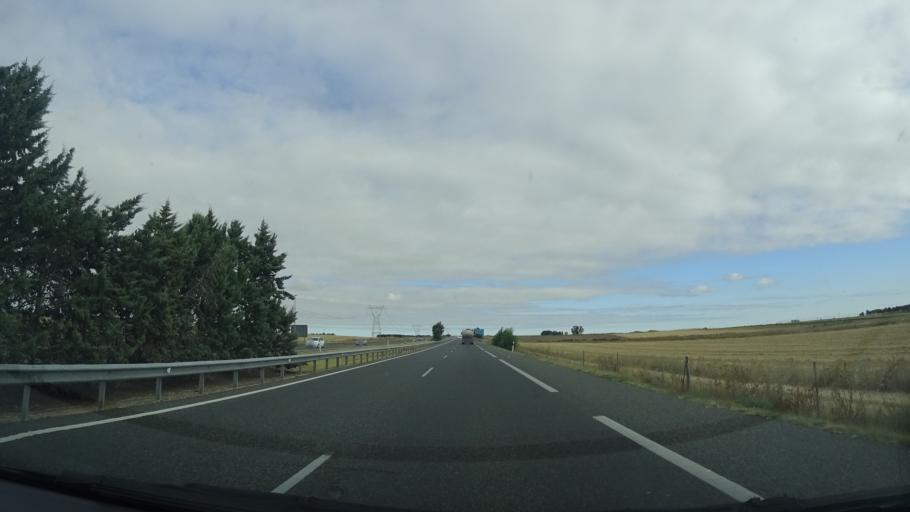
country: ES
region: Castille and Leon
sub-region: Provincia de Avila
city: Palacios de Goda
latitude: 41.1364
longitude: -4.7790
